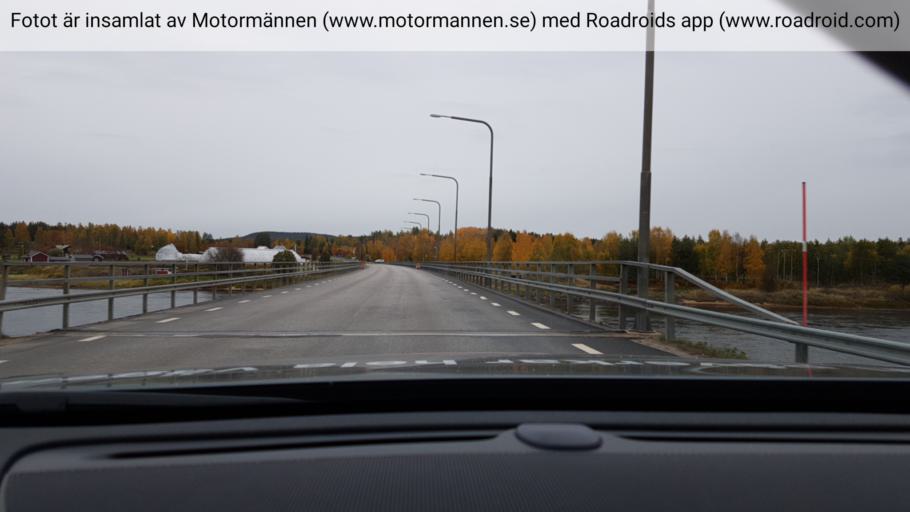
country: SE
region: Norrbotten
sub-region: Overkalix Kommun
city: OEverkalix
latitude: 66.3629
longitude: 22.8386
